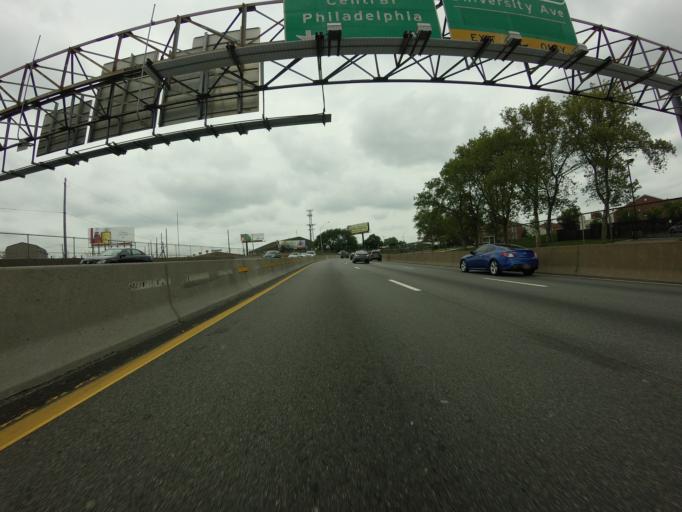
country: US
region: Pennsylvania
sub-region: Philadelphia County
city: Philadelphia
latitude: 39.9313
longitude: -75.1994
